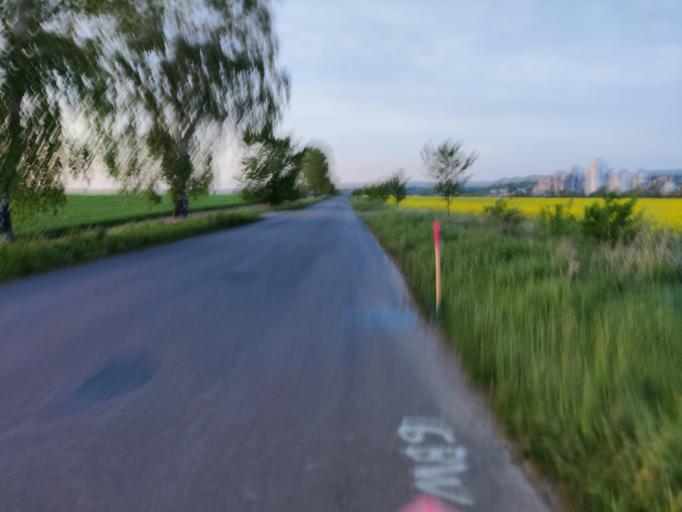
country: DE
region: Saxony-Anhalt
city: Karsdorf
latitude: 51.2602
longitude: 11.6448
